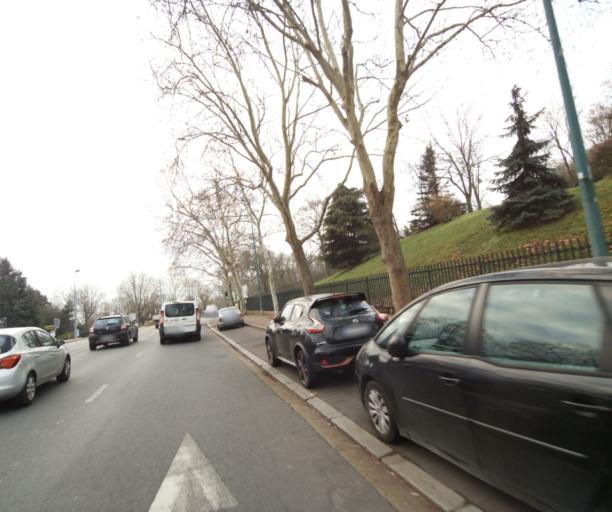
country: FR
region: Ile-de-France
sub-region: Departement des Hauts-de-Seine
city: Suresnes
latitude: 48.8763
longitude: 2.2173
